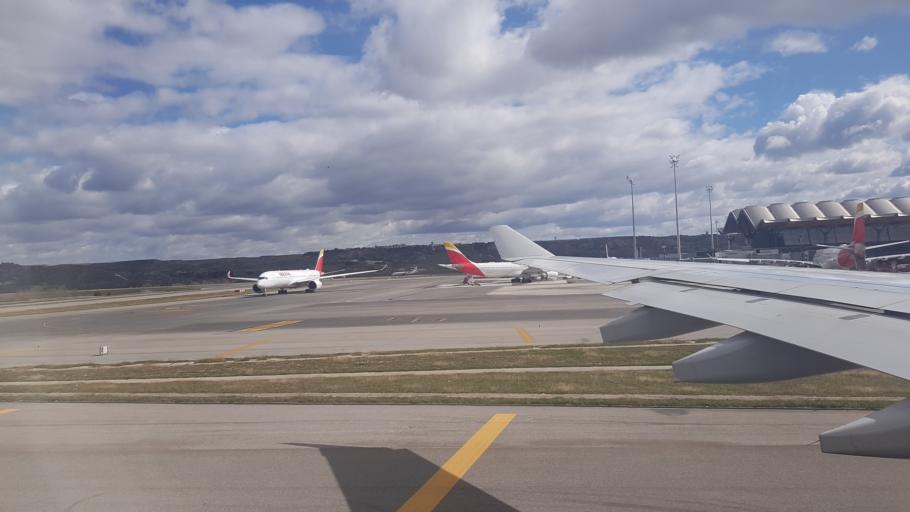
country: ES
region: Madrid
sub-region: Provincia de Madrid
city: Barajas de Madrid
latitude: 40.4994
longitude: -3.5712
